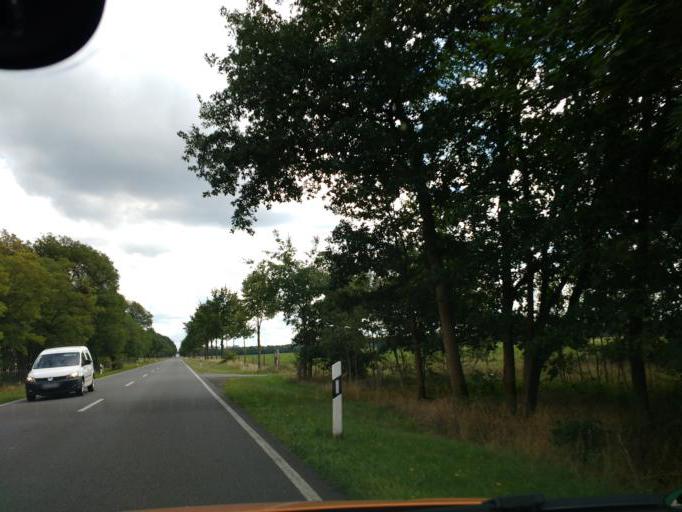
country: DE
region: Brandenburg
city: Marienwerder
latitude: 52.8564
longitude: 13.5527
